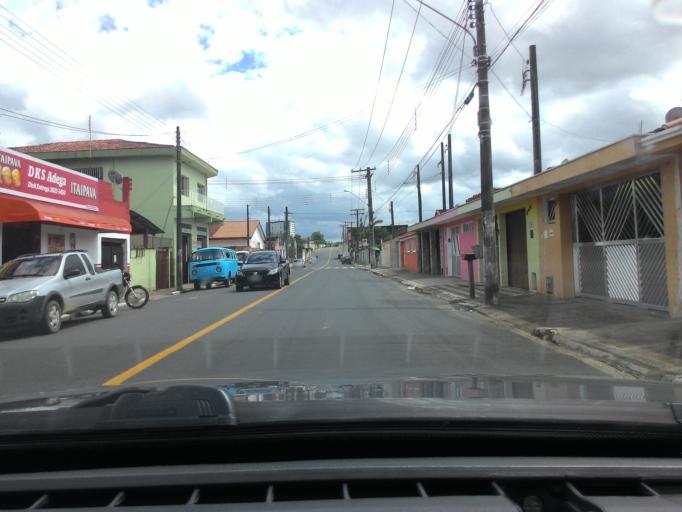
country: BR
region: Sao Paulo
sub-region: Registro
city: Registro
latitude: -24.5026
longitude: -47.8435
